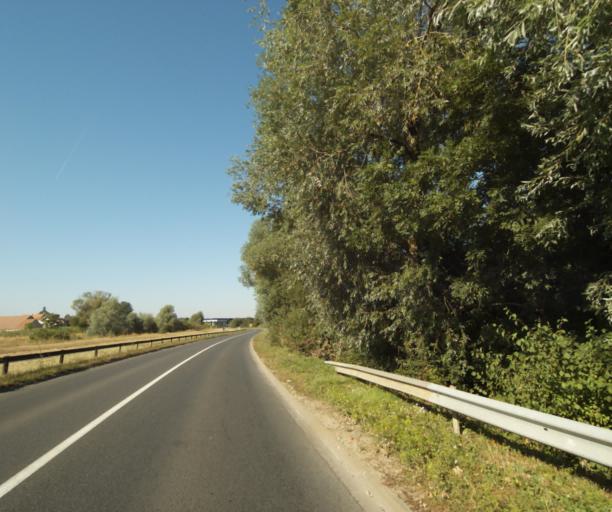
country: FR
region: Ile-de-France
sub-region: Departement de Seine-et-Marne
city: Moissy-Cramayel
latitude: 48.6350
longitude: 2.5757
